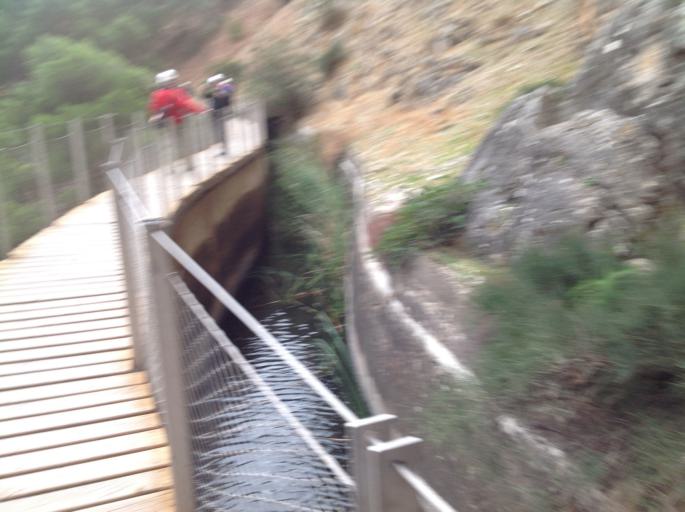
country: ES
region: Andalusia
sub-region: Provincia de Malaga
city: Ardales
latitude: 36.9291
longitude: -4.7838
